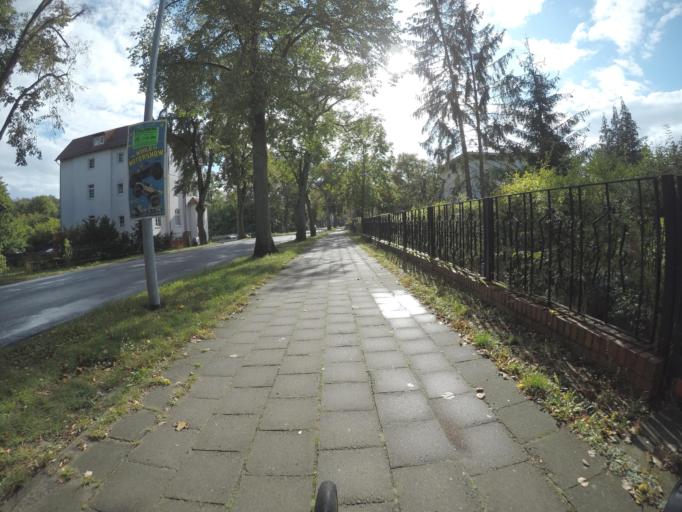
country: DE
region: Brandenburg
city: Strausberg
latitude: 52.5396
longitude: 13.8533
